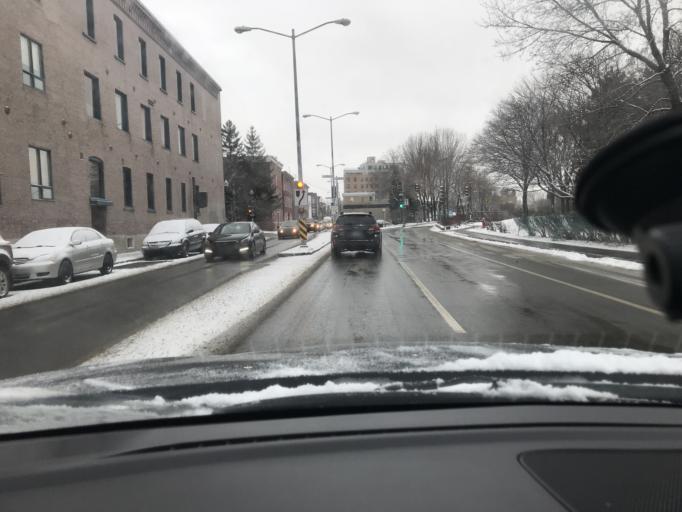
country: CA
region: Quebec
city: Quebec
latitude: 46.8167
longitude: -71.2257
